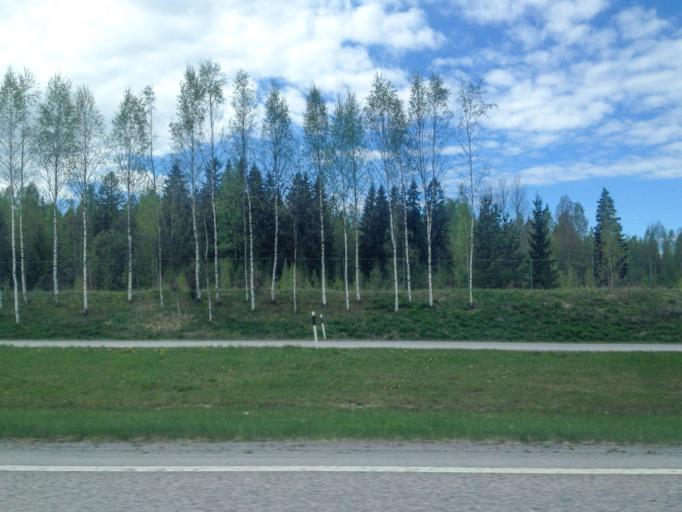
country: FI
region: Uusimaa
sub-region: Helsinki
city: Hyvinge
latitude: 60.6281
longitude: 24.8099
